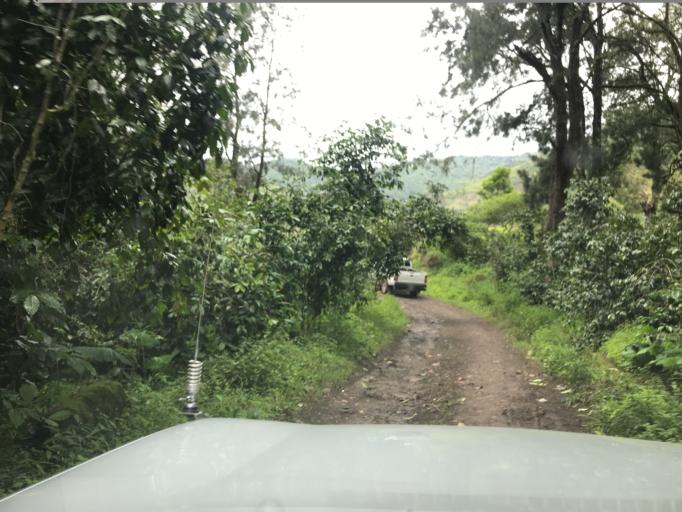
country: TL
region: Aileu
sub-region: Aileu Villa
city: Aileu
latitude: -8.8626
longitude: 125.5645
